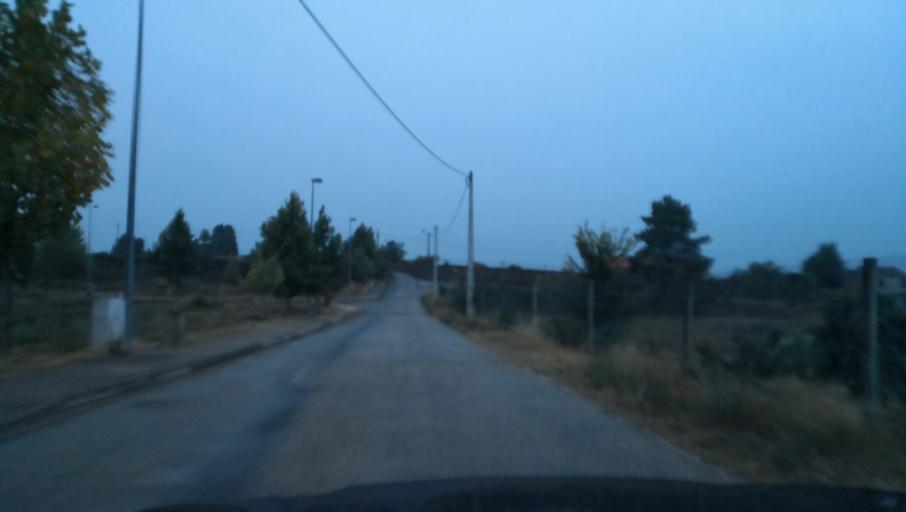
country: PT
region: Vila Real
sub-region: Sabrosa
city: Sabrosa
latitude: 41.2688
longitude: -7.6219
